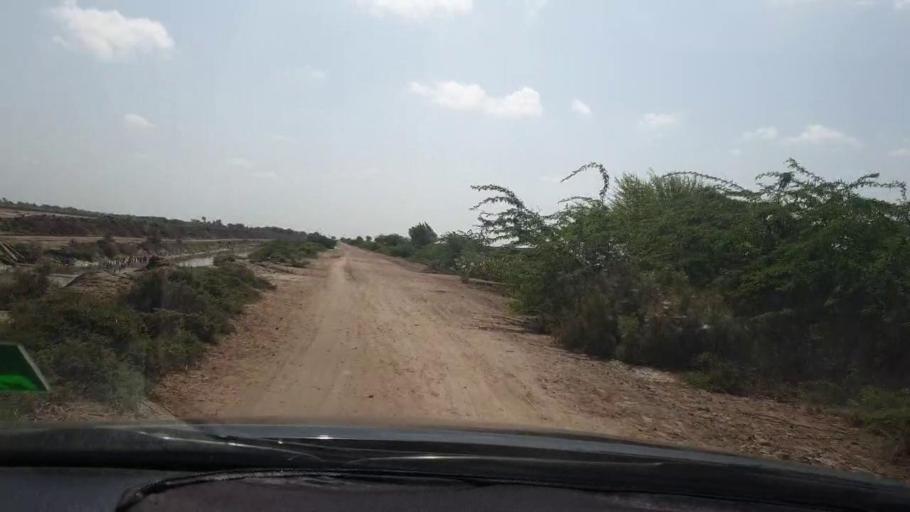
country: PK
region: Sindh
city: Tando Bago
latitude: 24.8464
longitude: 69.0367
